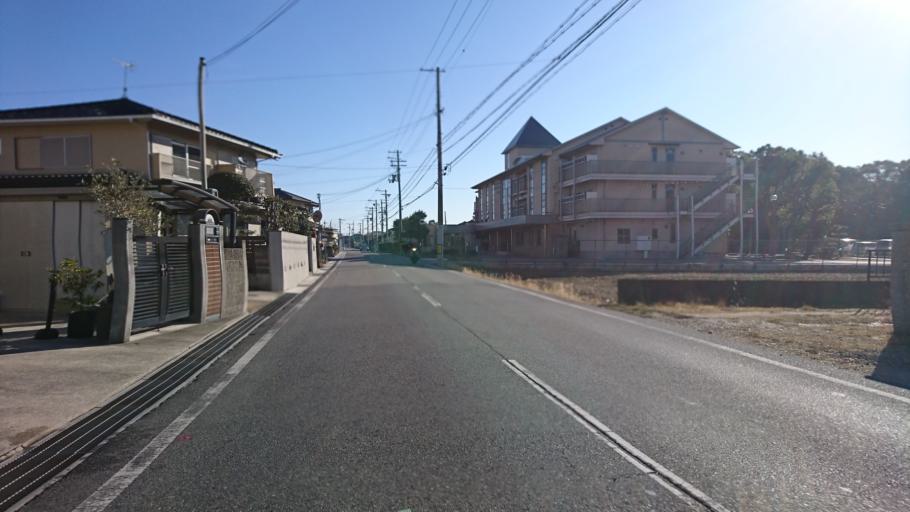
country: JP
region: Hyogo
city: Kakogawacho-honmachi
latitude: 34.7525
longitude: 134.8809
